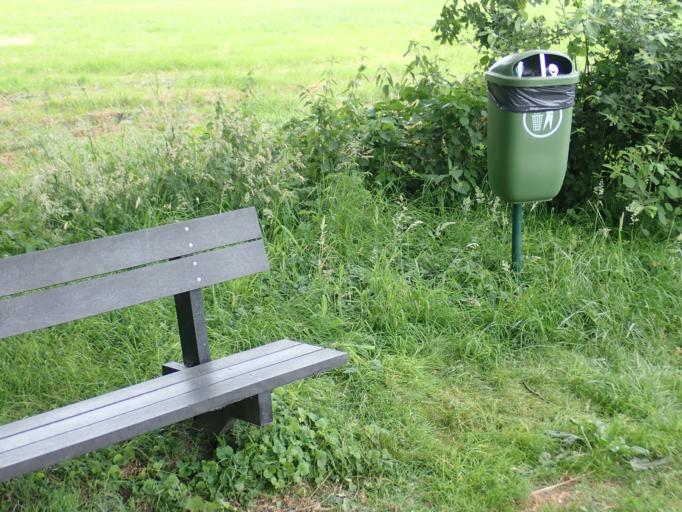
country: BE
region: Flanders
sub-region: Provincie Antwerpen
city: Merksplas
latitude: 51.3674
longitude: 4.8756
